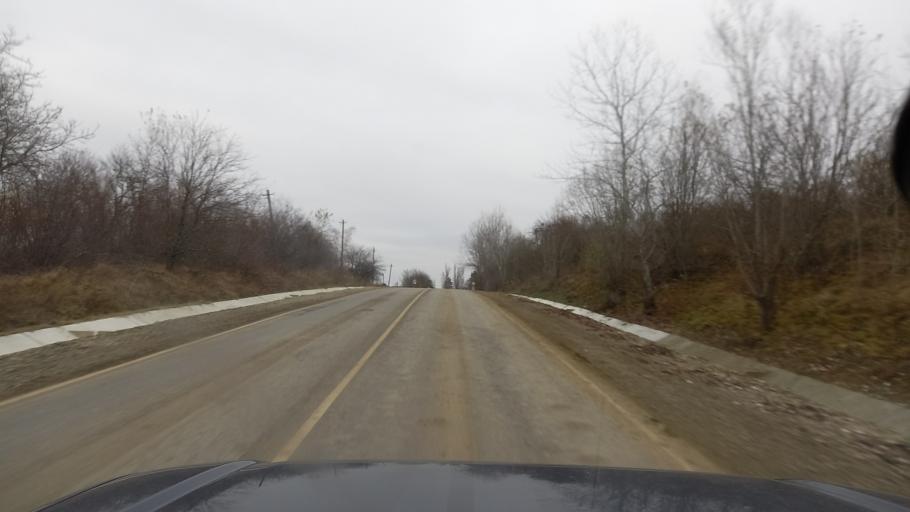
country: RU
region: Krasnodarskiy
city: Saratovskaya
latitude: 44.5460
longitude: 39.2850
